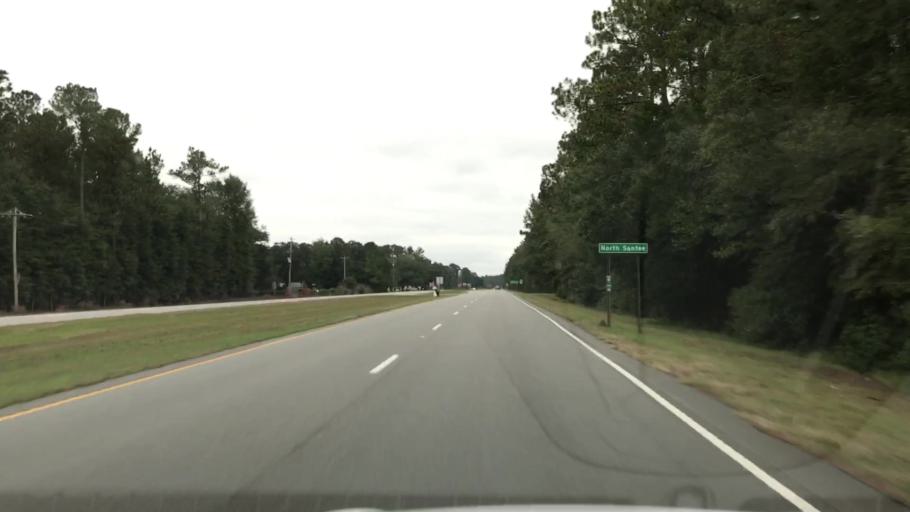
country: US
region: South Carolina
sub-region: Georgetown County
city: Georgetown
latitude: 33.2183
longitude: -79.3796
